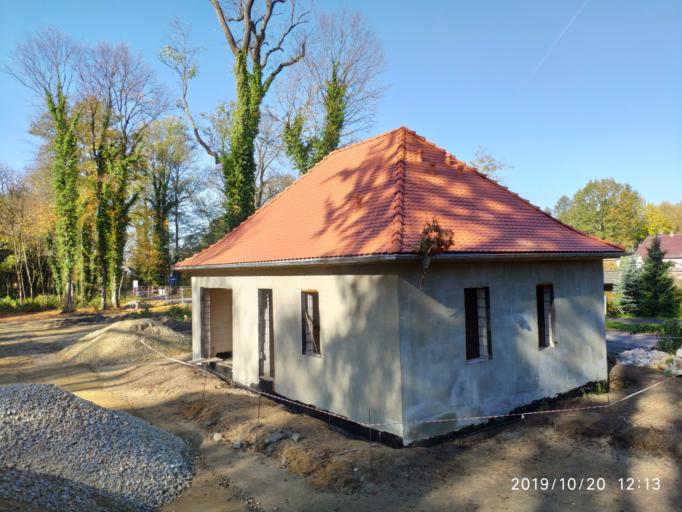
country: PL
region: Lubusz
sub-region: Zielona Gora
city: Zielona Gora
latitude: 51.8616
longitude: 15.5655
